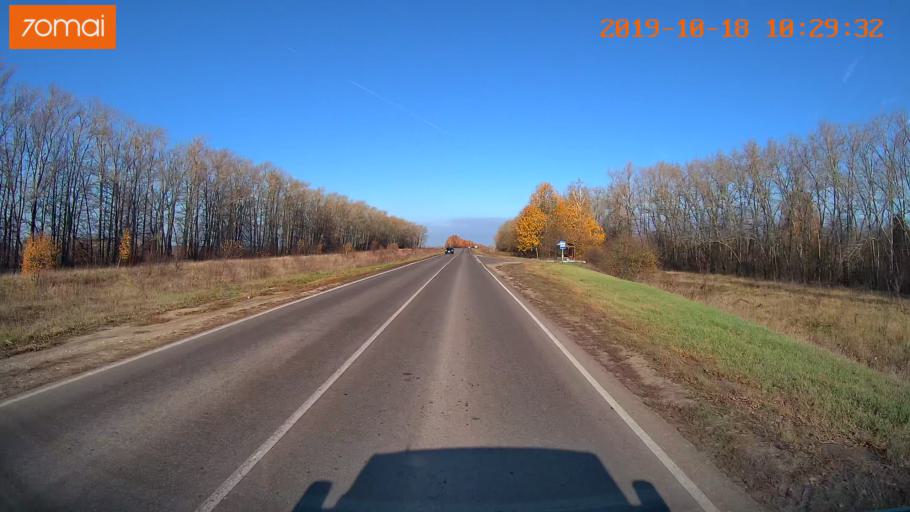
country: RU
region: Tula
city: Kurkino
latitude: 53.4526
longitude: 38.6552
